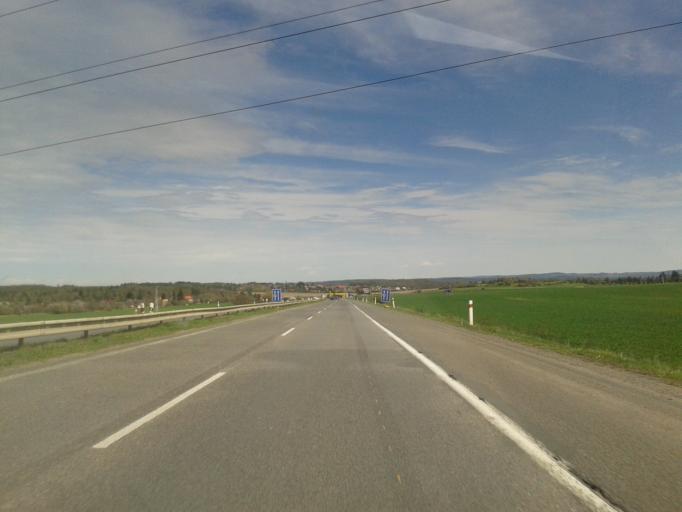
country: CZ
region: Central Bohemia
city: Vsenory
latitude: 49.8948
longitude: 14.3103
